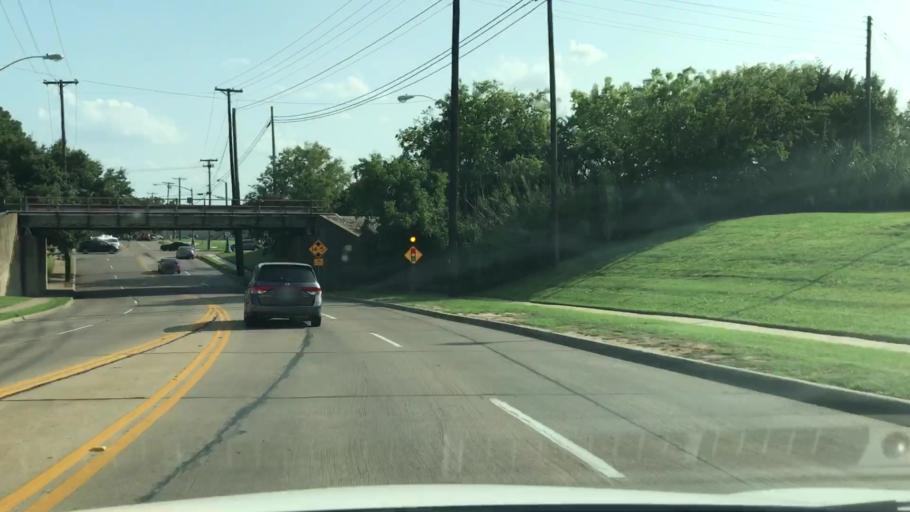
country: US
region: Texas
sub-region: Dallas County
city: Irving
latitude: 32.8156
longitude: -96.9499
